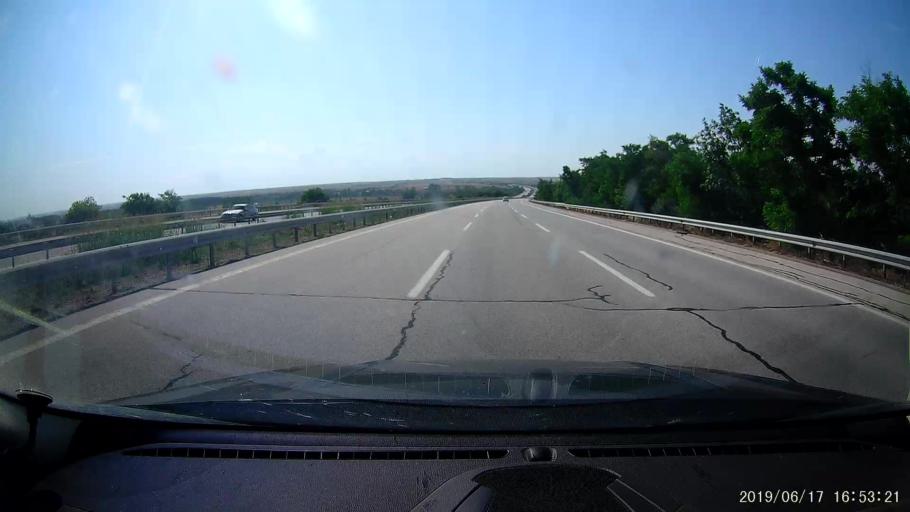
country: TR
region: Kirklareli
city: Inece
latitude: 41.5626
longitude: 27.0255
